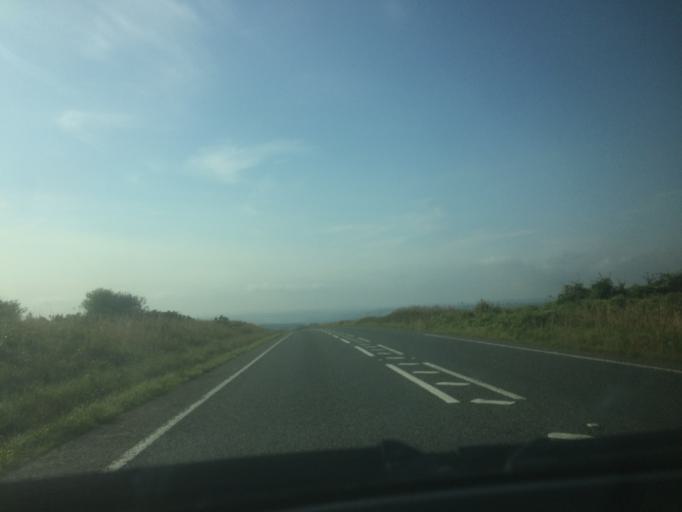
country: GB
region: England
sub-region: Cornwall
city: Callington
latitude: 50.4818
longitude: -4.2861
